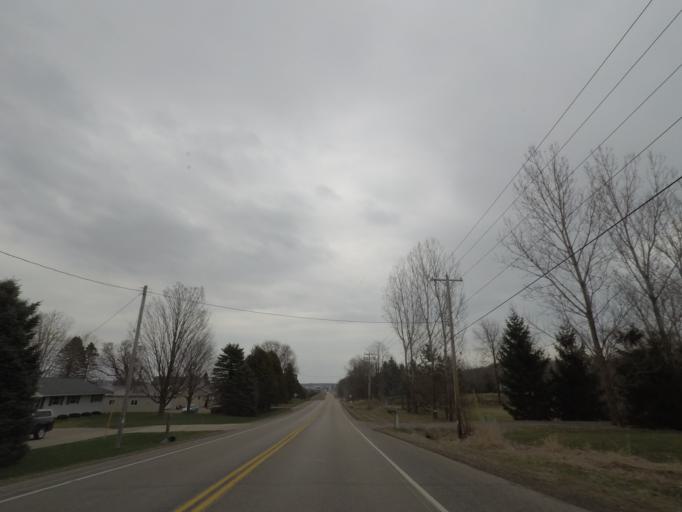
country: US
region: Wisconsin
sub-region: Dane County
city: Middleton
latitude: 43.1111
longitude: -89.5497
